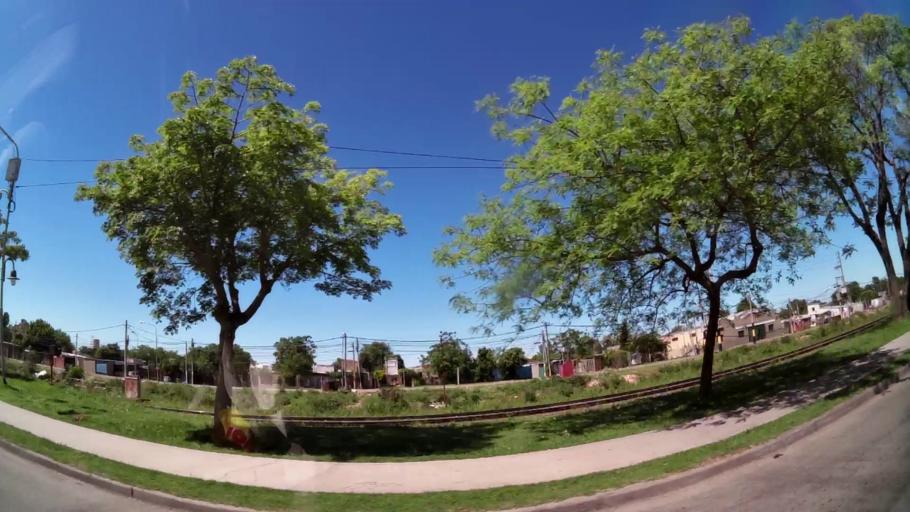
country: AR
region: Buenos Aires
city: Hurlingham
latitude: -34.5030
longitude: -58.6333
